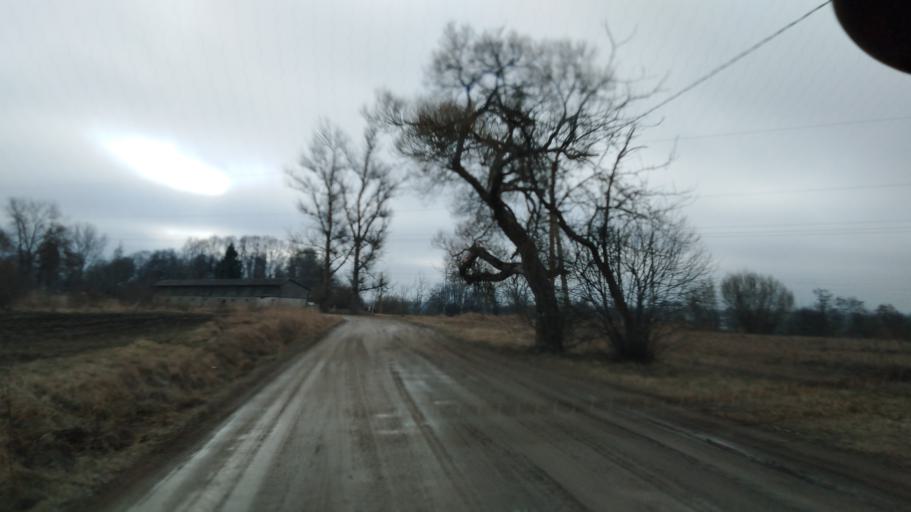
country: LV
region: Kuldigas Rajons
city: Kuldiga
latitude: 56.9848
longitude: 21.9710
